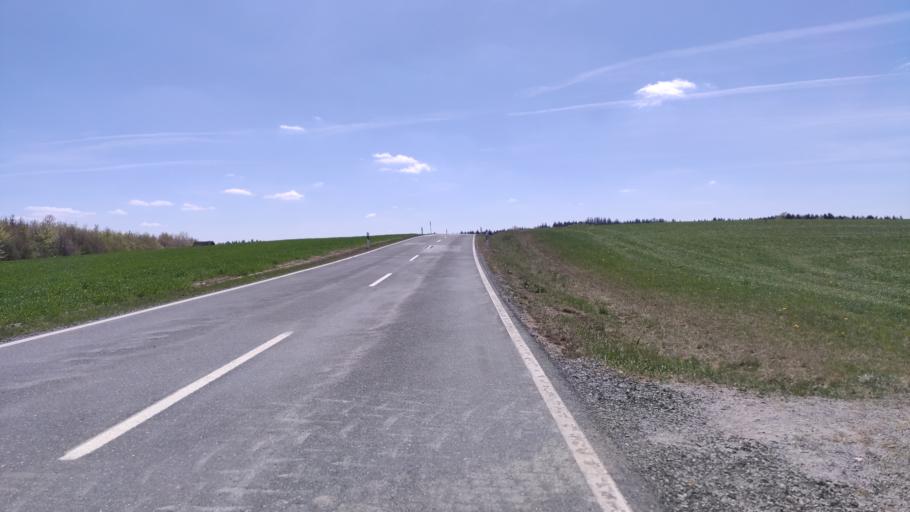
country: DE
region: Bavaria
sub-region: Upper Franconia
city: Tschirn
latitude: 50.3852
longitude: 11.4536
